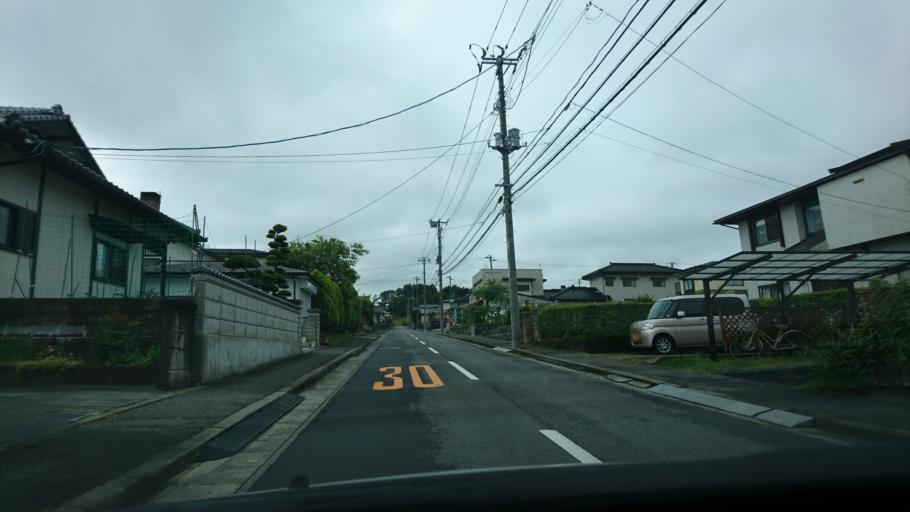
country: JP
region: Iwate
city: Ichinoseki
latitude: 38.9065
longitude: 141.1401
